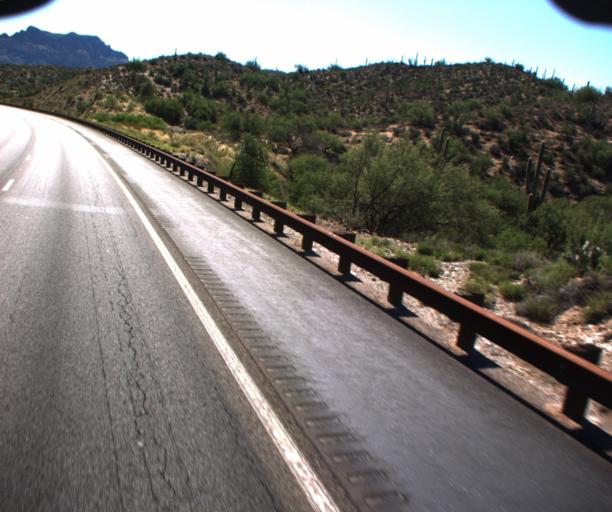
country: US
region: Arizona
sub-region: Pinal County
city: Gold Camp
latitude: 33.2727
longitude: -111.2181
